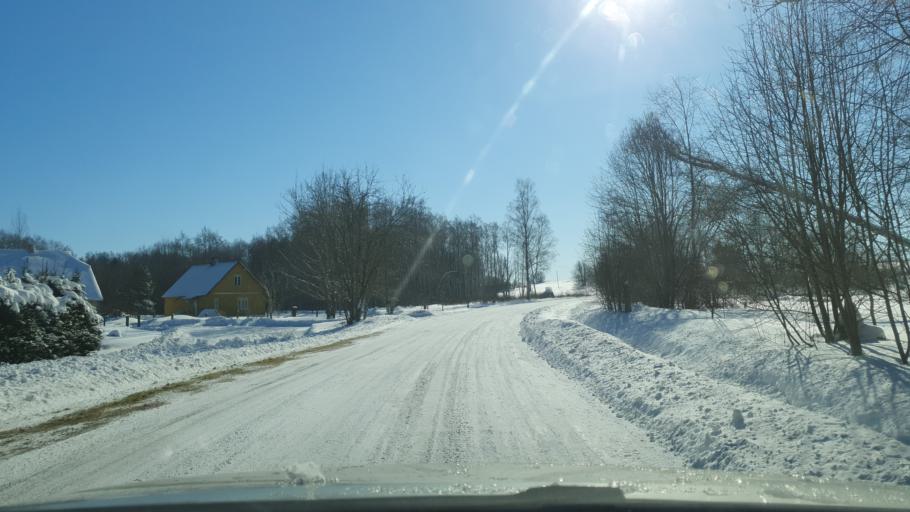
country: EE
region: Laeaene-Virumaa
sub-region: Haljala vald
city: Haljala
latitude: 59.5531
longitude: 26.1331
